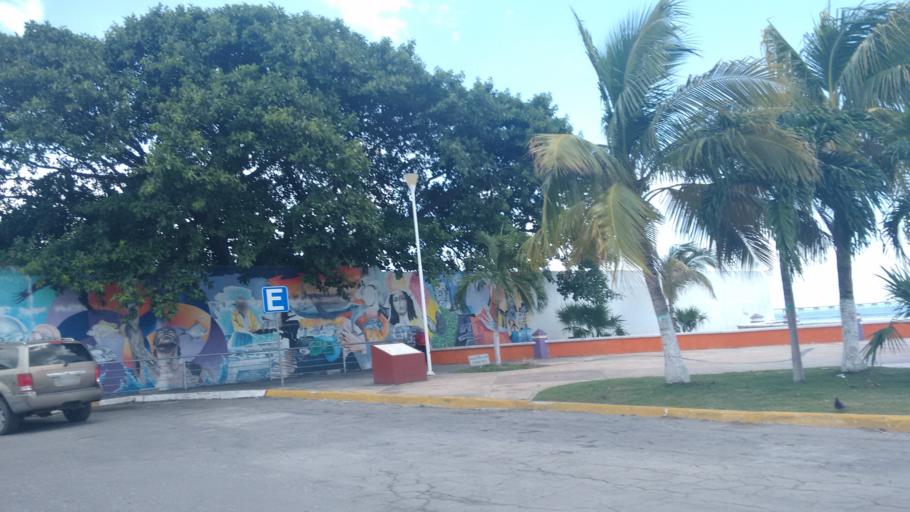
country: MX
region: Campeche
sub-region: Carmen
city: Ciudad del Carmen
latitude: 18.6343
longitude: -91.8338
